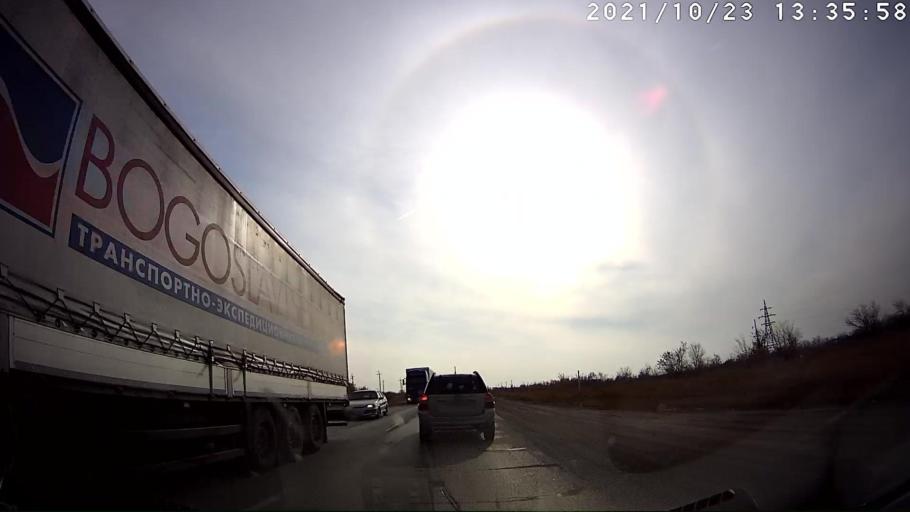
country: RU
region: Volgograd
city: Vodstroy
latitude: 48.8547
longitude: 44.5615
